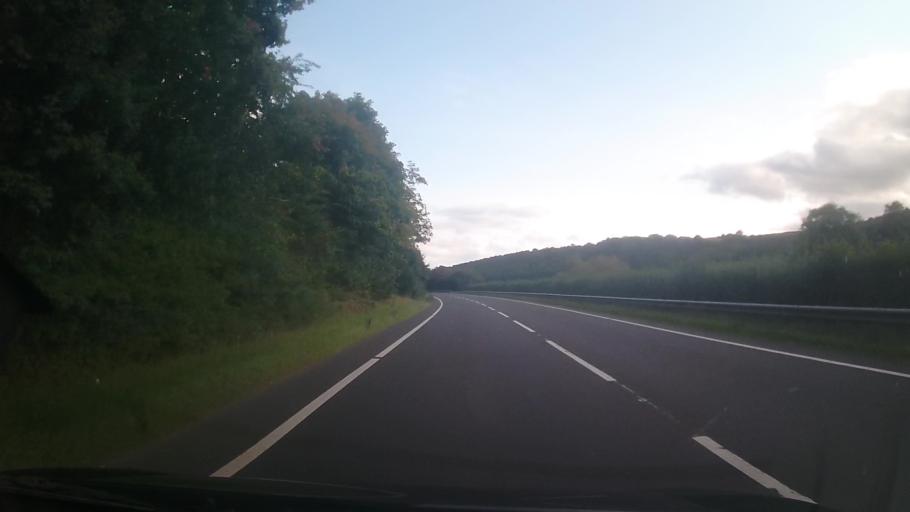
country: GB
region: England
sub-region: Shropshire
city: Craven Arms
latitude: 52.4213
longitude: -2.8225
